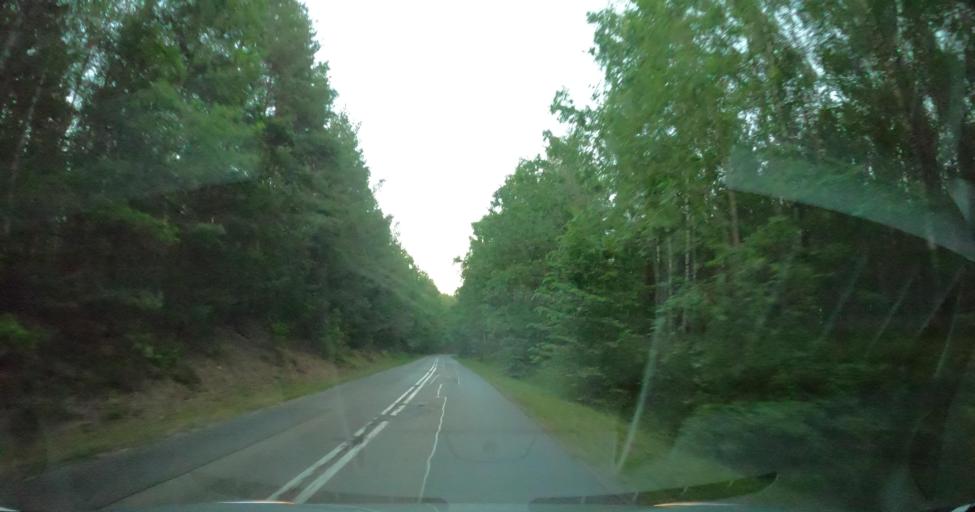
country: PL
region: Pomeranian Voivodeship
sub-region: Powiat wejherowski
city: Linia
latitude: 54.4615
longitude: 17.9981
